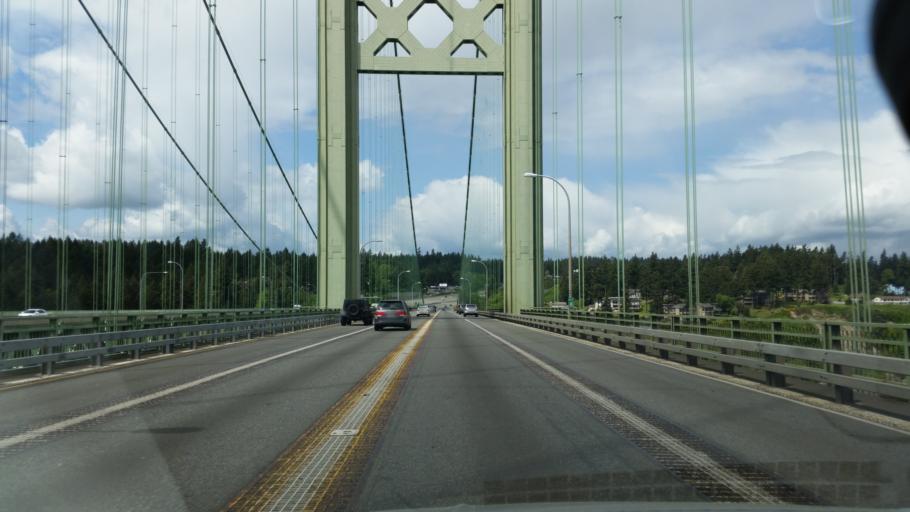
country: US
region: Washington
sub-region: Pierce County
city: Wollochet
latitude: 47.2707
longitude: -122.5532
